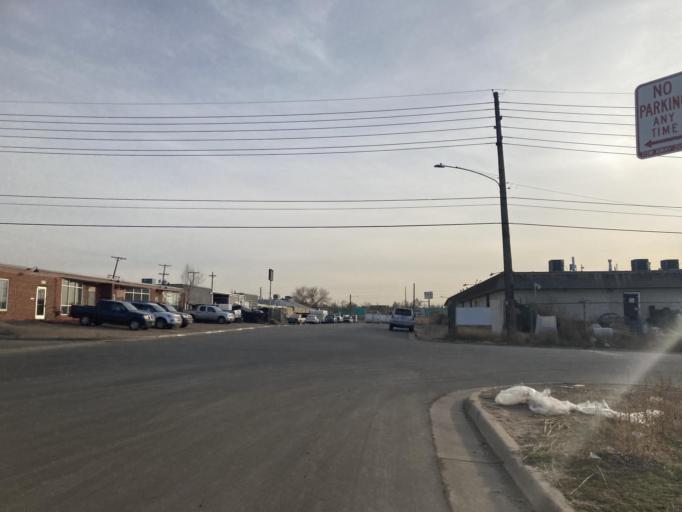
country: US
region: Colorado
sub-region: Adams County
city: Commerce City
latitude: 39.7791
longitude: -104.9442
